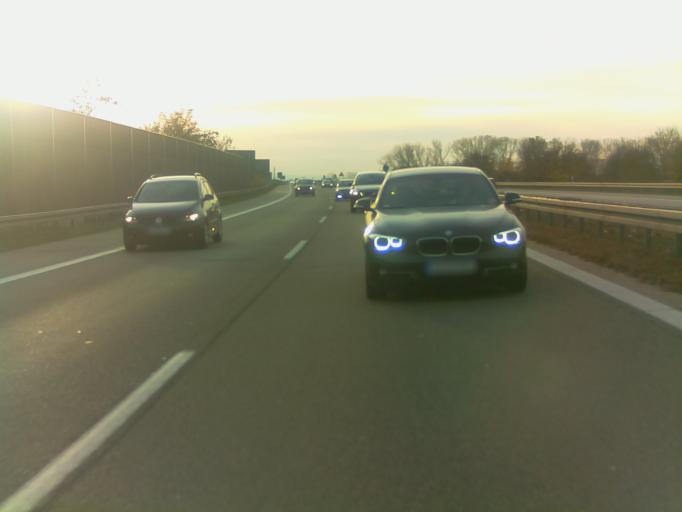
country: DE
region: Hesse
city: Lampertheim
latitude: 49.5518
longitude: 8.4271
